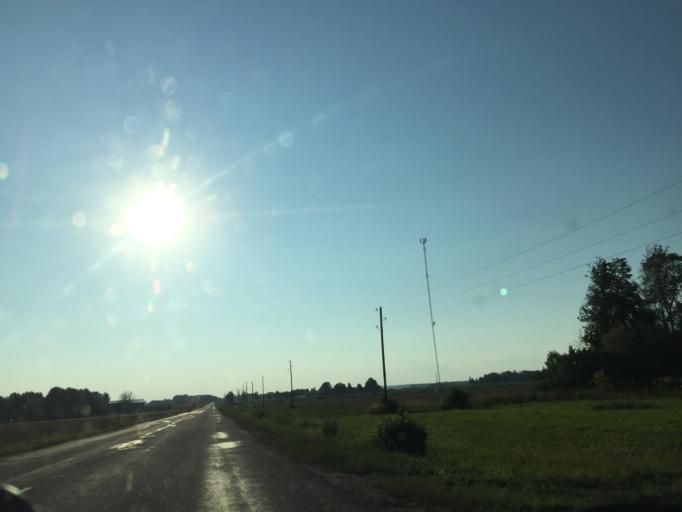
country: LV
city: Tervete
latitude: 56.4376
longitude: 23.5076
